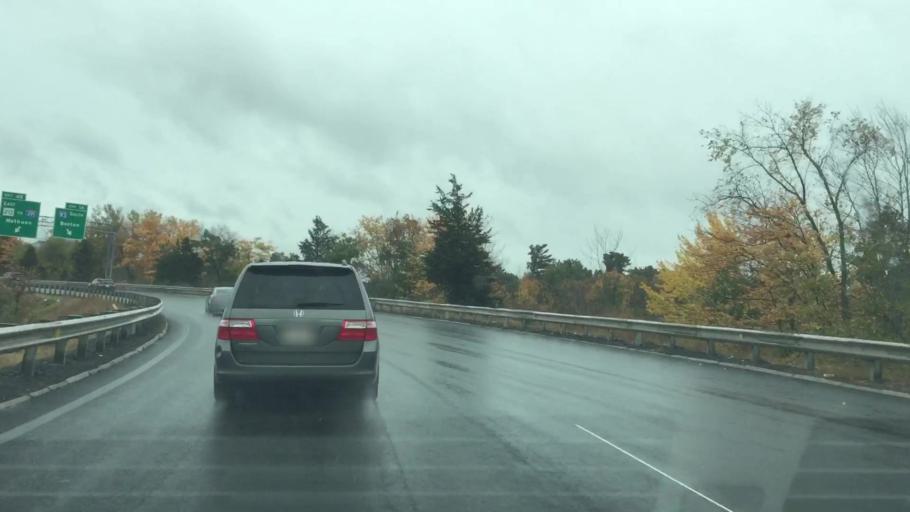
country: US
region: Massachusetts
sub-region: Essex County
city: Methuen
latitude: 42.7352
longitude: -71.2033
